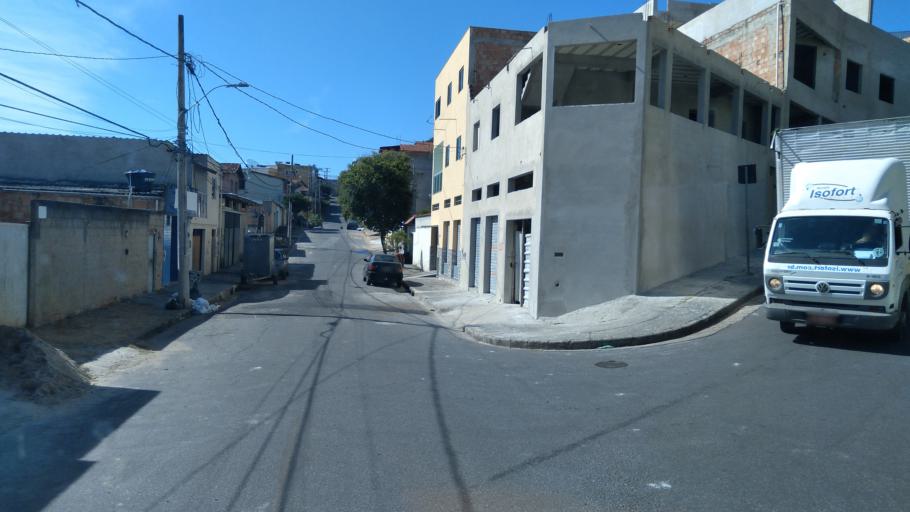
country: BR
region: Minas Gerais
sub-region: Belo Horizonte
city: Belo Horizonte
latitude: -19.8452
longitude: -43.9044
